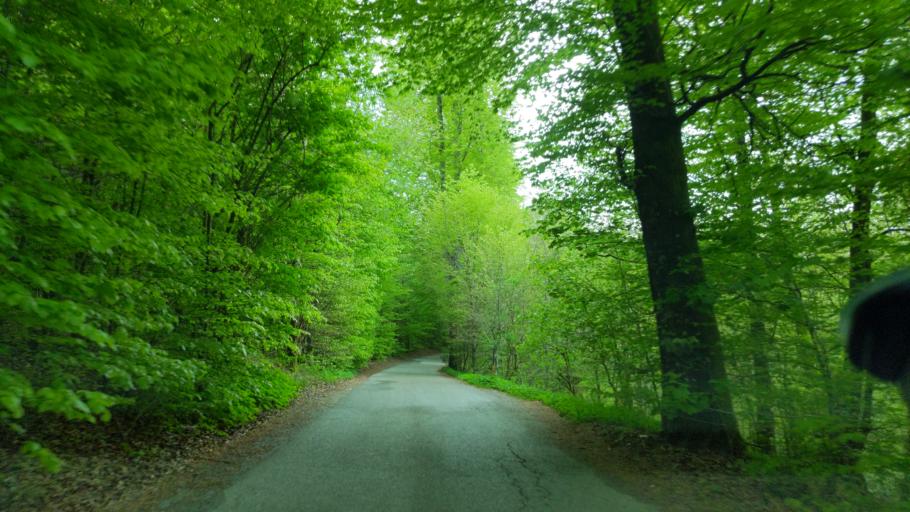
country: DE
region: Bavaria
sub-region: Upper Bavaria
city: Ebersberg
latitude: 48.1104
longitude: 11.9904
